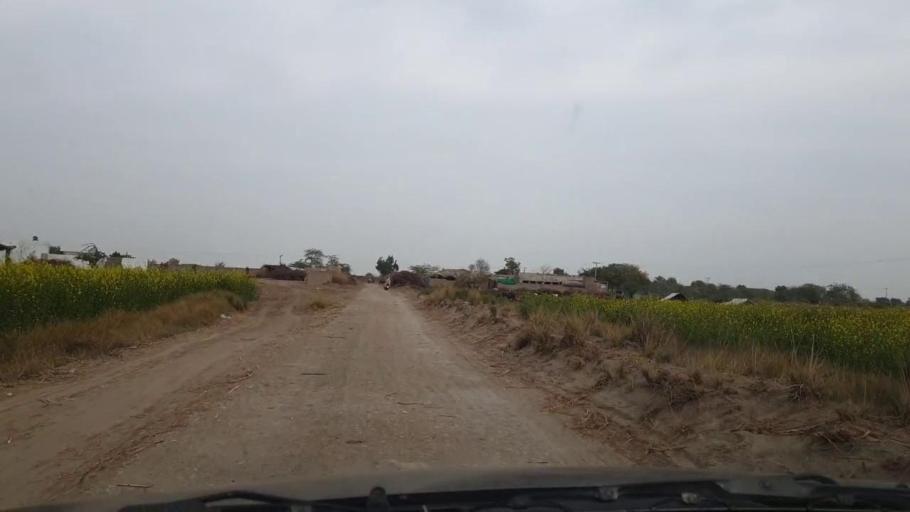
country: PK
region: Sindh
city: Sanghar
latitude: 26.1170
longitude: 68.8963
